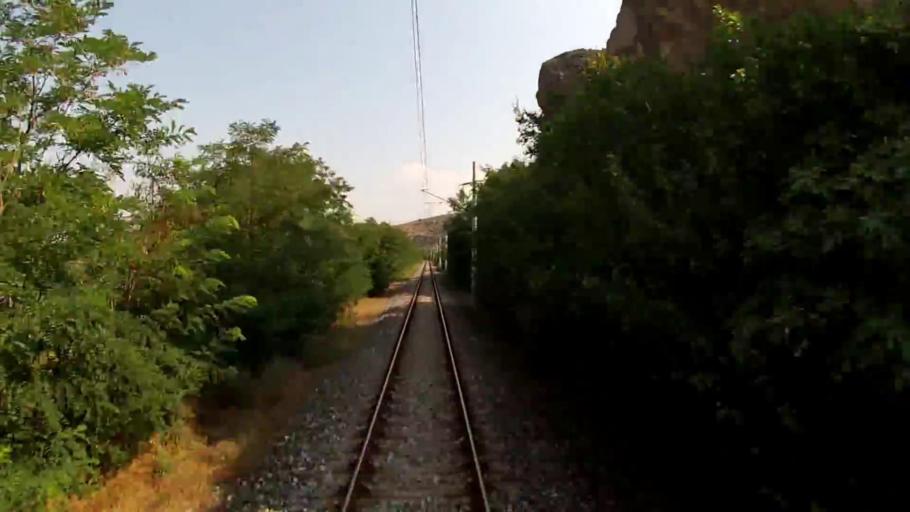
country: BG
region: Blagoevgrad
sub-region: Obshtina Sandanski
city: Sandanski
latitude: 41.4853
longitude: 23.2735
